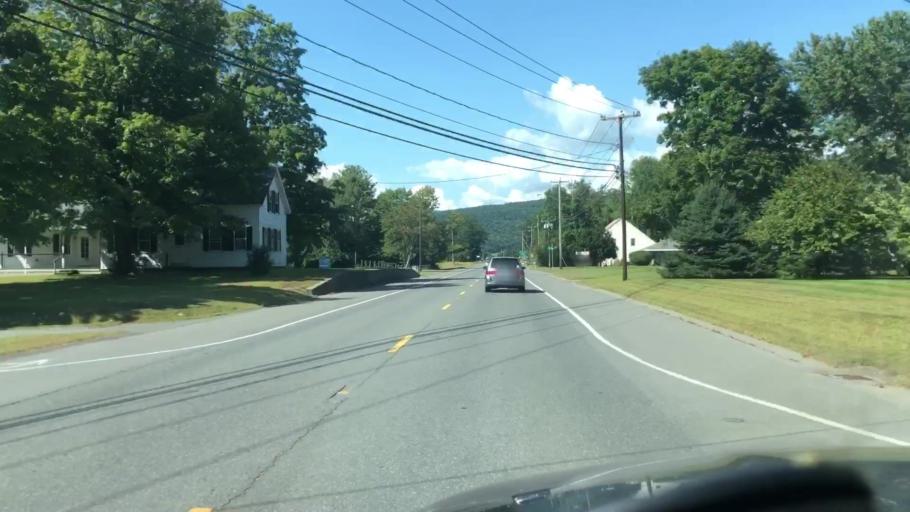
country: US
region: Massachusetts
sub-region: Franklin County
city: Bernardston
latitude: 42.6699
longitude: -72.5347
